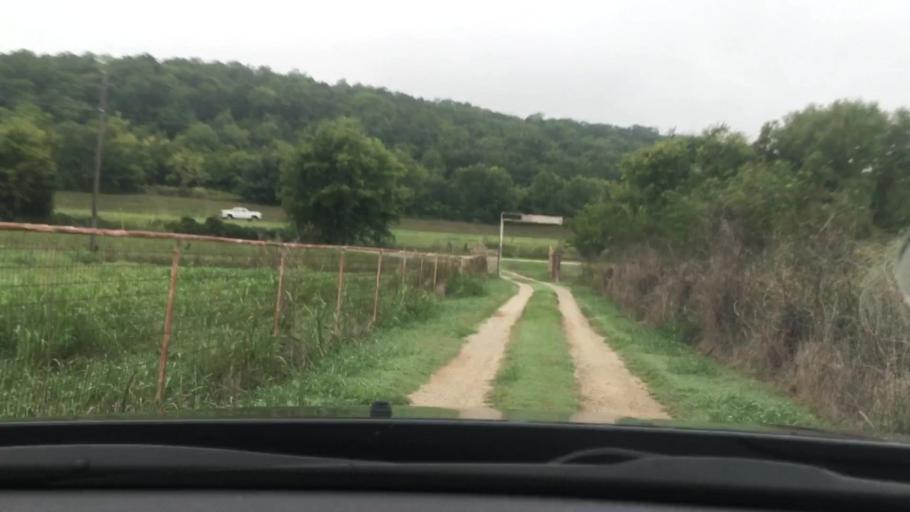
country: US
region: Oklahoma
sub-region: Murray County
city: Davis
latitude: 34.4675
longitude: -97.1499
